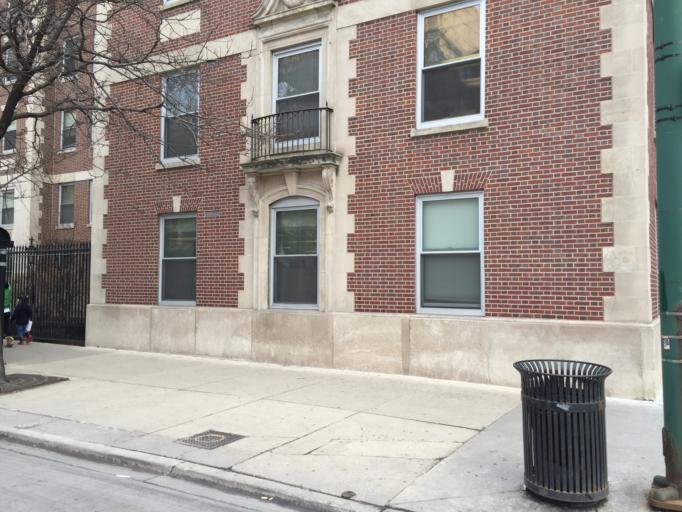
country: US
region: Illinois
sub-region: Cook County
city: Chicago
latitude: 41.8950
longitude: -87.6326
